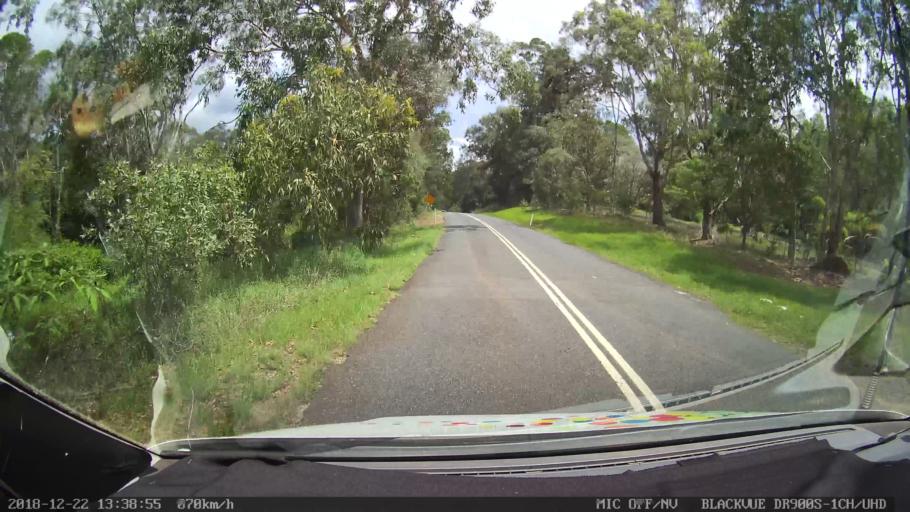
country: AU
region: New South Wales
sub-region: Clarence Valley
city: Coutts Crossing
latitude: -29.9053
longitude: 152.7861
